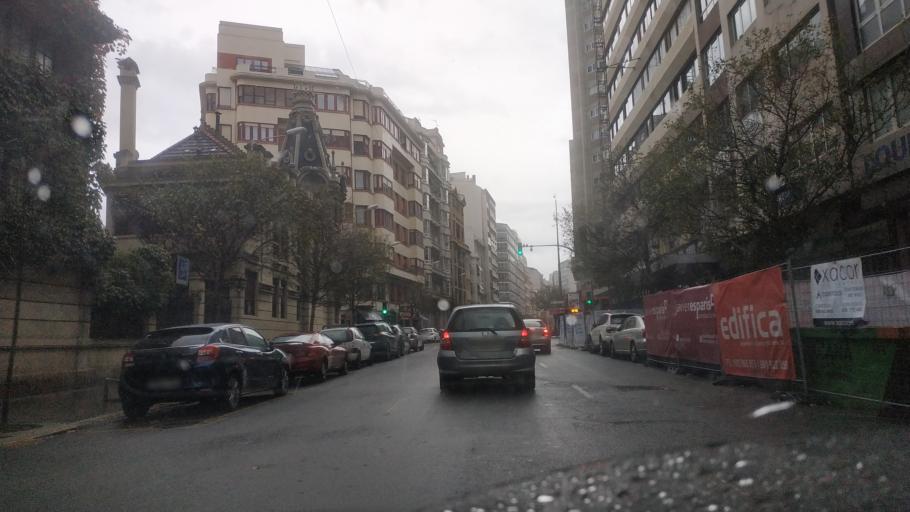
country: ES
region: Galicia
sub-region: Provincia da Coruna
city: A Coruna
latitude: 43.3652
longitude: -8.4083
